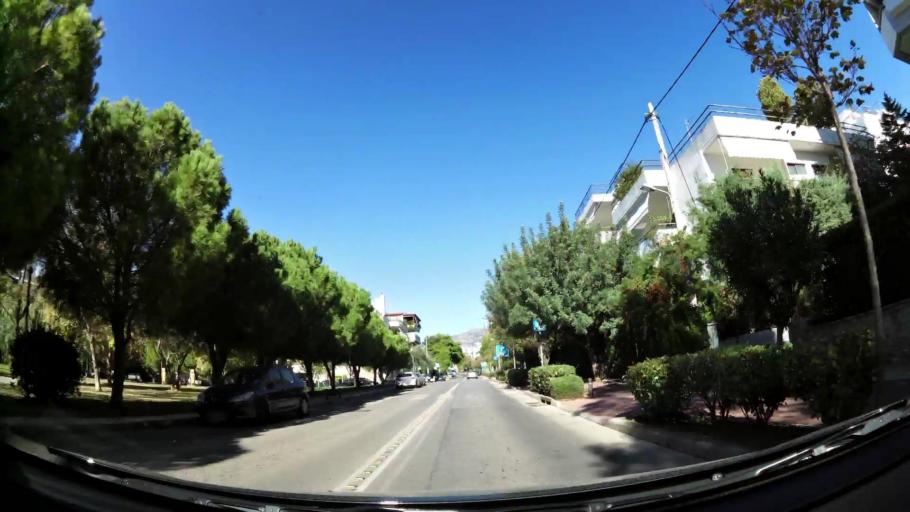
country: GR
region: Attica
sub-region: Nomarchia Athinas
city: Vrilissia
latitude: 38.0320
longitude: 23.8355
